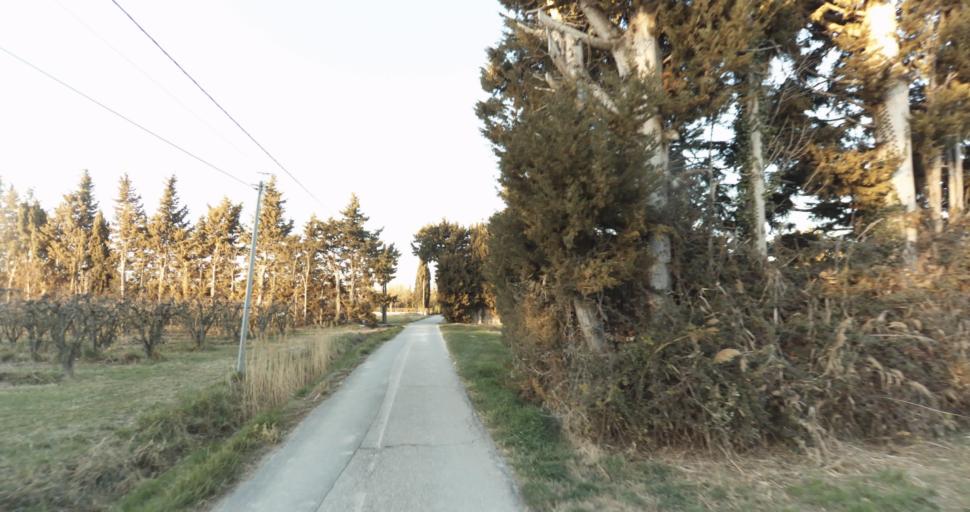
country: FR
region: Provence-Alpes-Cote d'Azur
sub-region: Departement des Bouches-du-Rhone
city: Rognonas
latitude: 43.8939
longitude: 4.7777
